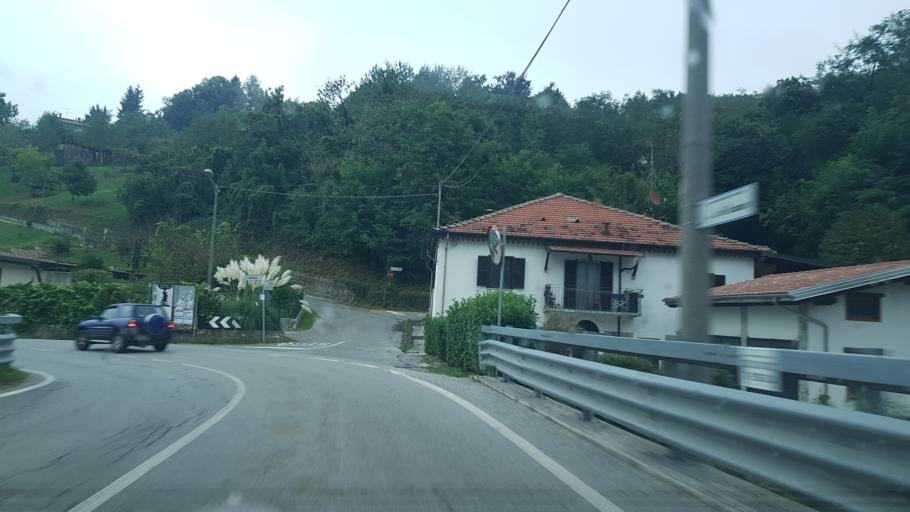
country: IT
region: Piedmont
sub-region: Provincia di Cuneo
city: Frabosa Sottana
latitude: 44.3236
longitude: 7.8012
